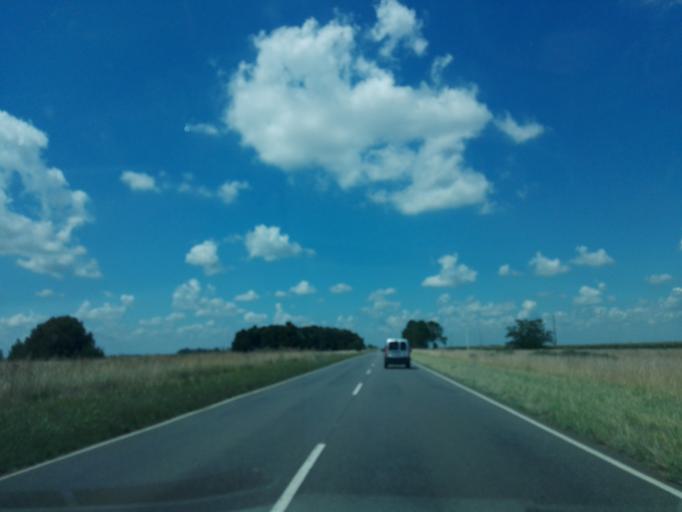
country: AR
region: Buenos Aires
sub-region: Partido de General Belgrano
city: General Belgrano
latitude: -35.9134
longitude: -58.6194
